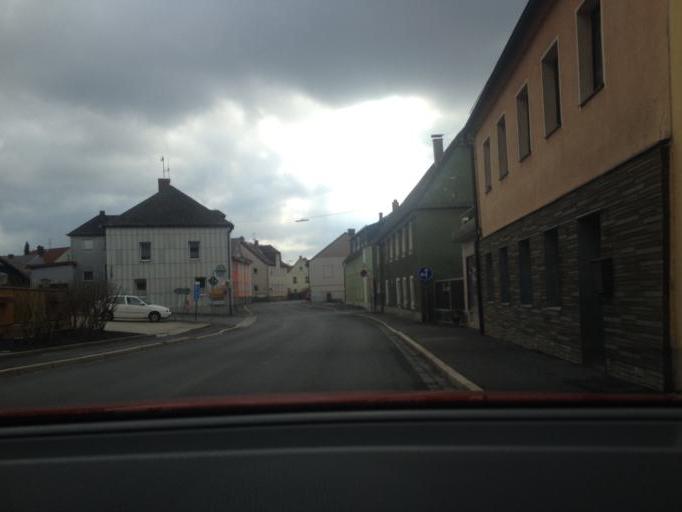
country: DE
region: Bavaria
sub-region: Upper Franconia
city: Thiersheim
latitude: 50.0762
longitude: 12.1286
